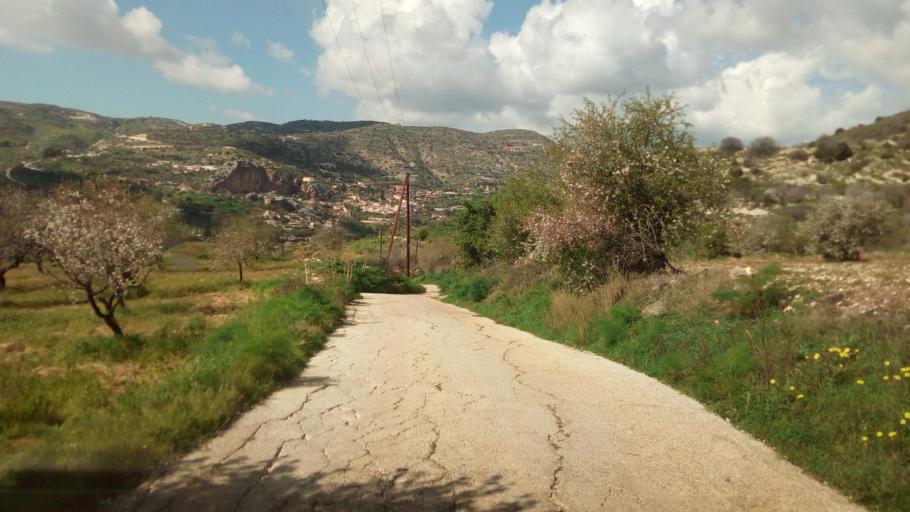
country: CY
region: Pafos
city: Mesogi
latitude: 34.7906
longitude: 32.5387
